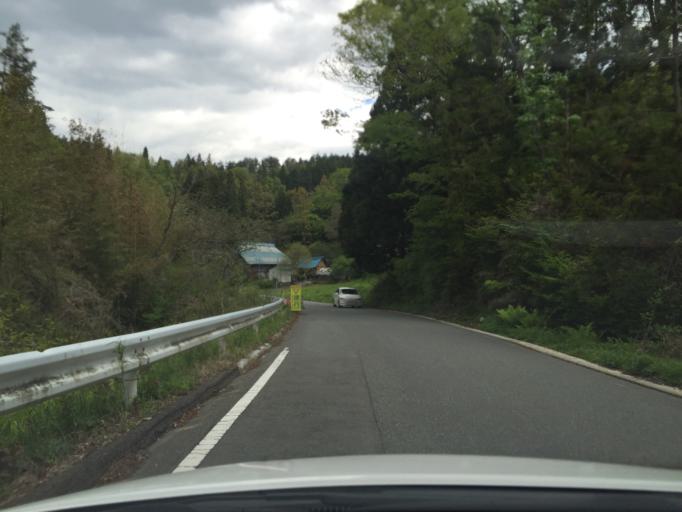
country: JP
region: Fukushima
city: Hobaramachi
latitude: 37.7222
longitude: 140.6435
